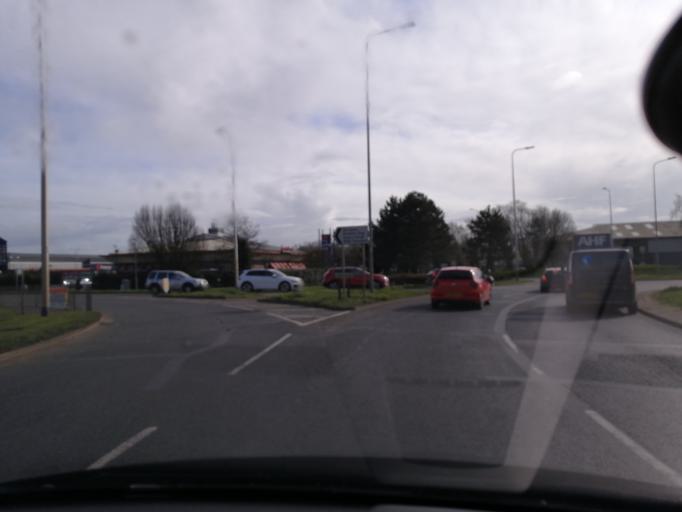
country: GB
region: England
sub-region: Peterborough
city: Peterborough
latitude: 52.5763
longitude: -0.2219
